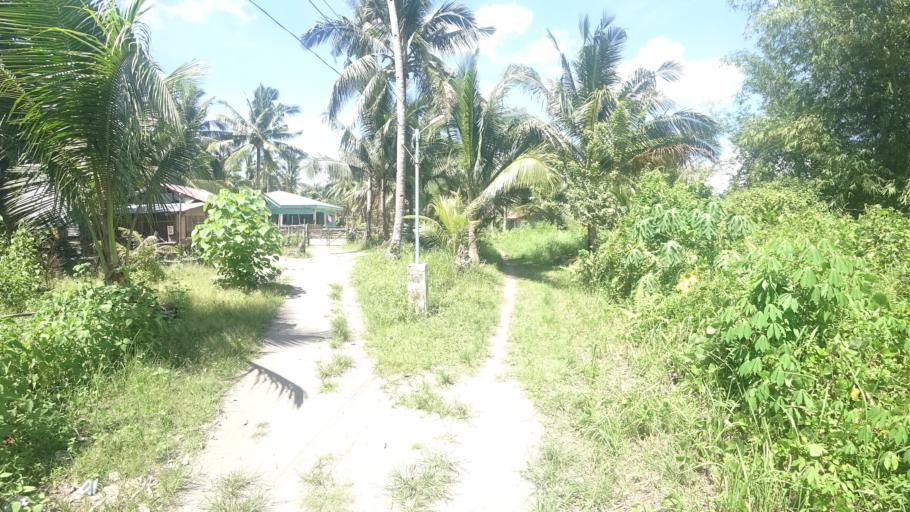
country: PH
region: Eastern Visayas
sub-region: Province of Leyte
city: Liberty
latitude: 10.8836
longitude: 125.0058
